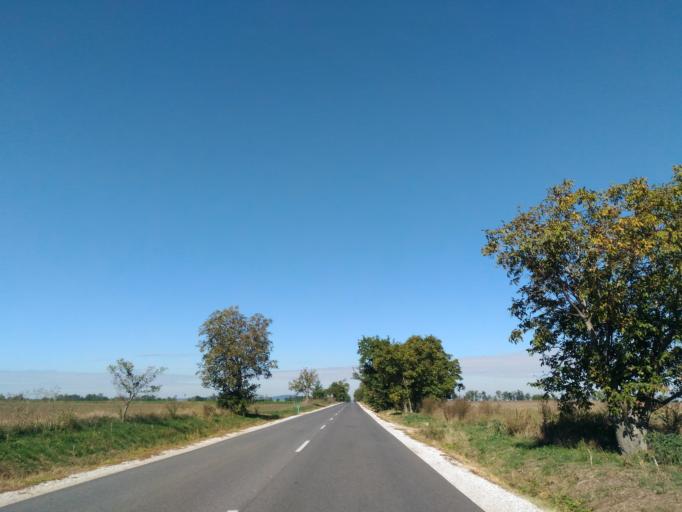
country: HU
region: Fejer
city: Kapolnasnyek
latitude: 47.1892
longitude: 18.7077
